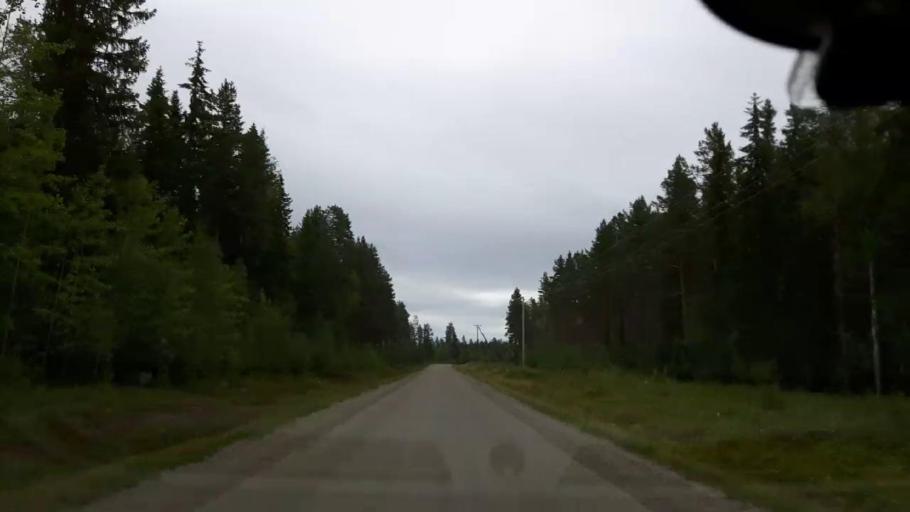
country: SE
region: Vaesternorrland
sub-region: Ange Kommun
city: Fransta
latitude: 62.8552
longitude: 16.0143
